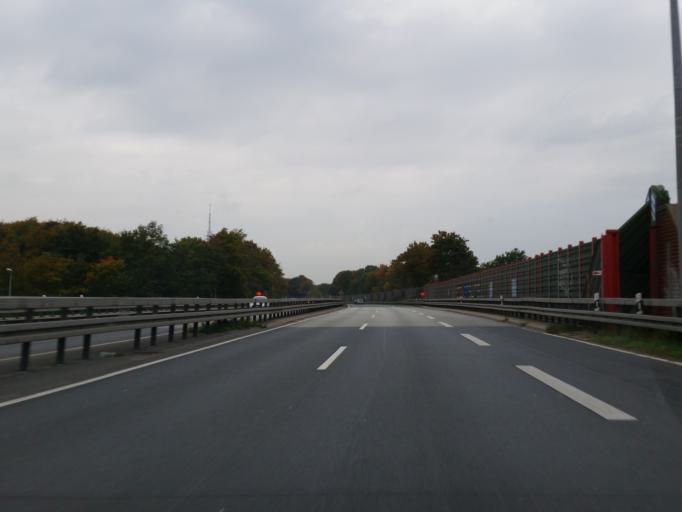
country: DE
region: Lower Saxony
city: Isernhagen Farster Bauerschaft
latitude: 52.4077
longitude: 9.8226
